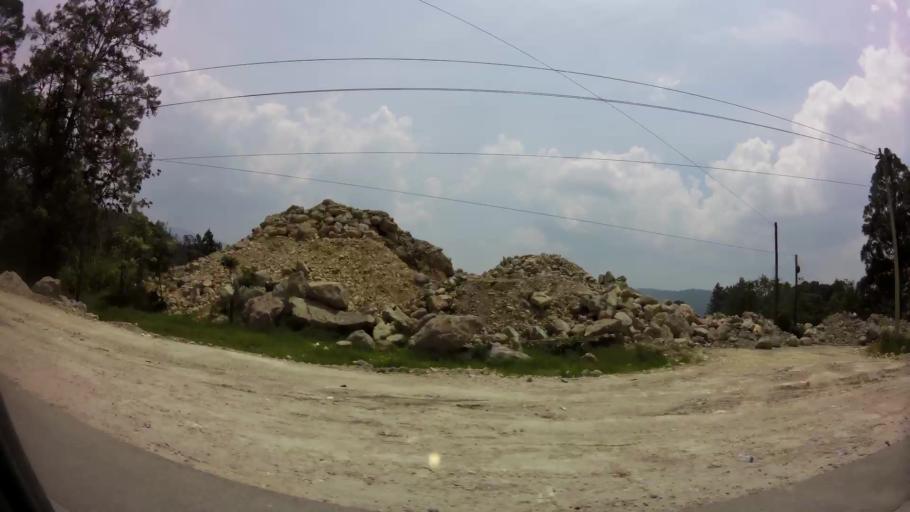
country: HN
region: Comayagua
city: El Socorro
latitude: 14.6534
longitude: -87.9368
